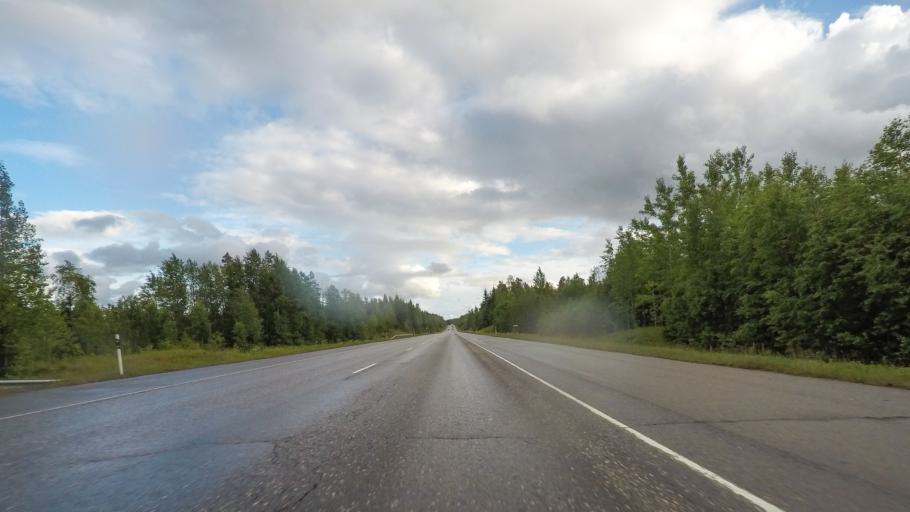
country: FI
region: Paijanne Tavastia
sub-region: Lahti
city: Heinola
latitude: 61.3251
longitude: 26.0414
